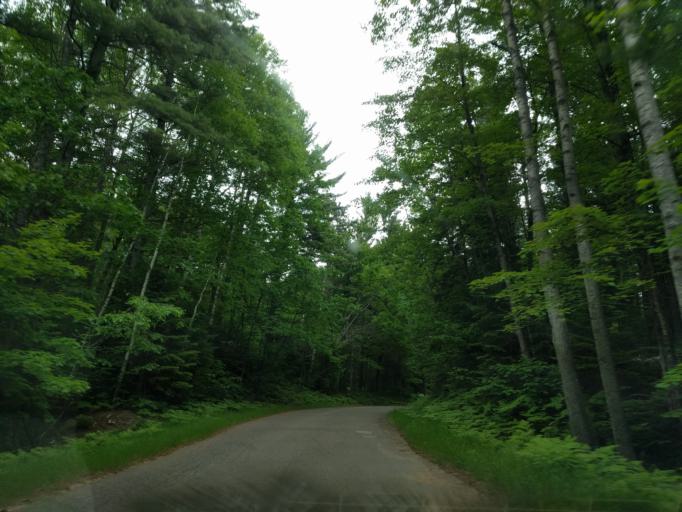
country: US
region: Michigan
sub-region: Marquette County
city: Trowbridge Park
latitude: 46.5741
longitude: -87.4766
